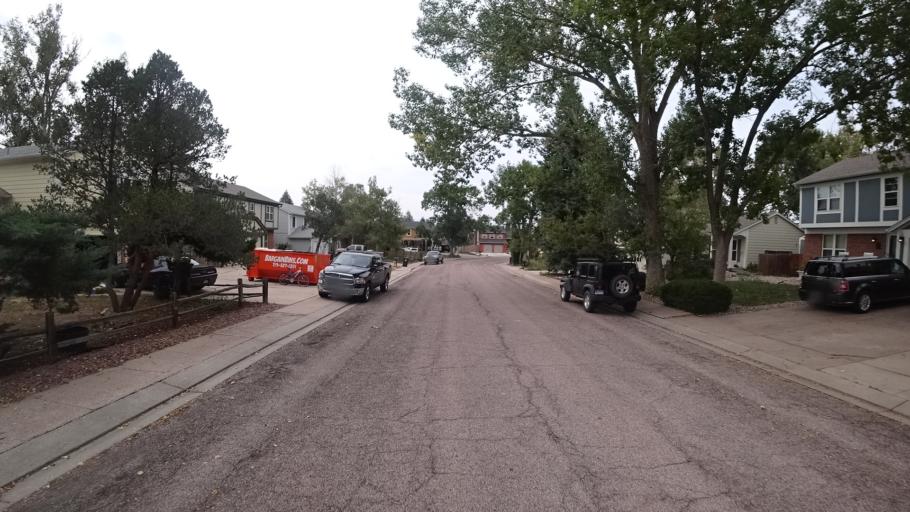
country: US
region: Colorado
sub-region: El Paso County
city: Cimarron Hills
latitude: 38.9019
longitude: -104.7328
